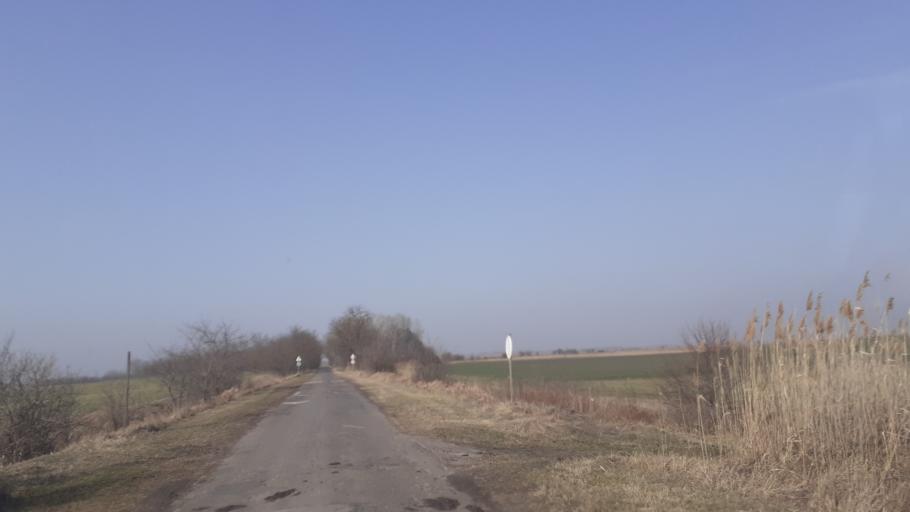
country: HU
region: Pest
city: Dabas
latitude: 47.0849
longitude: 19.2422
